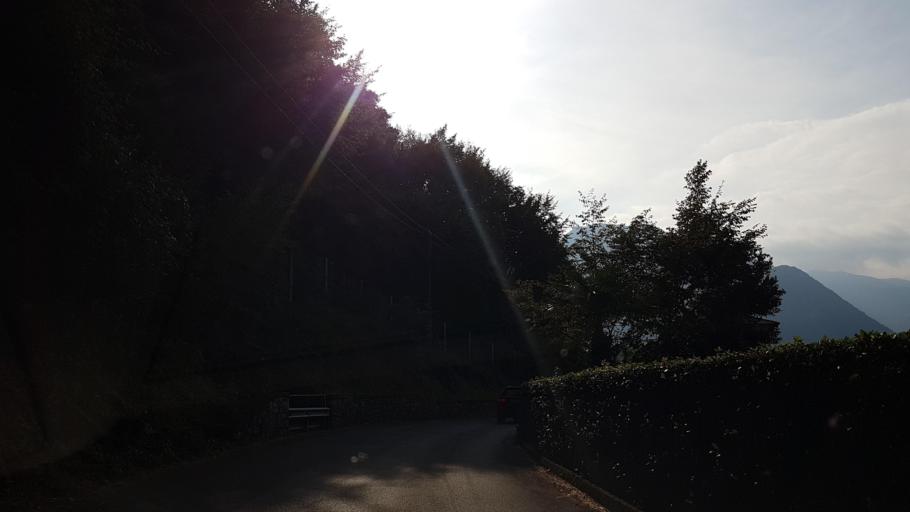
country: IT
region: Lombardy
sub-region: Provincia di Como
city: Colonno
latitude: 45.9389
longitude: 9.1629
